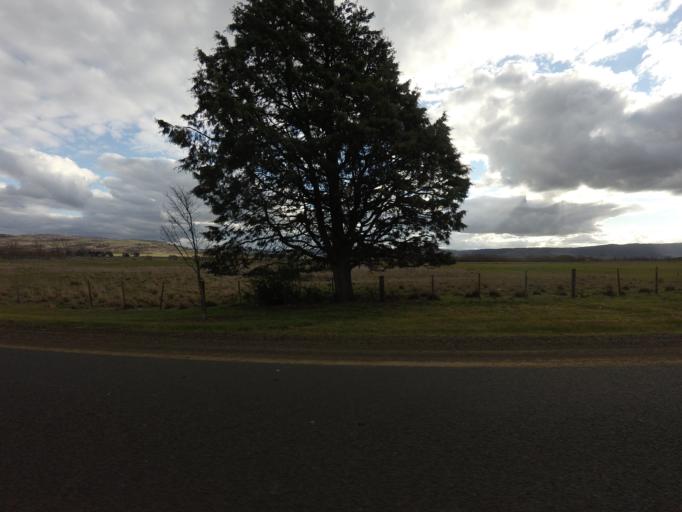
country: AU
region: Tasmania
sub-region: Northern Midlands
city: Evandale
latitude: -42.0235
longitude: 147.4930
